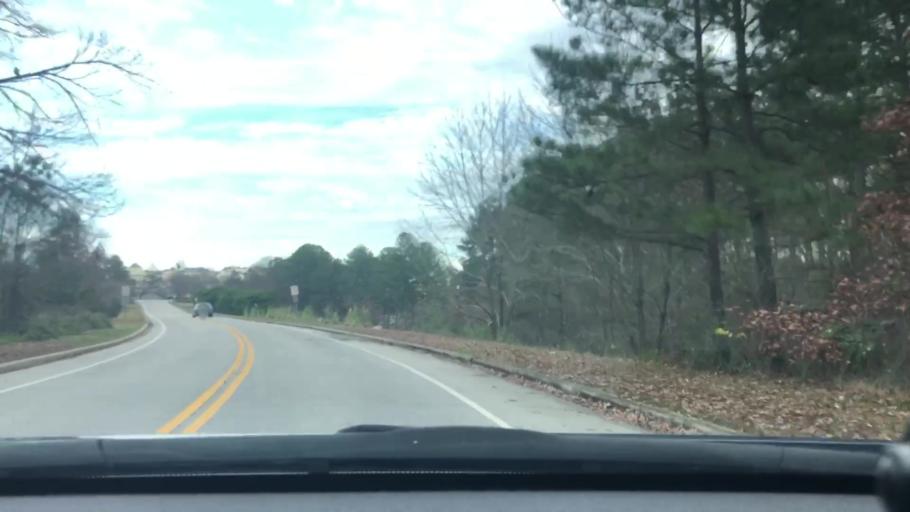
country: US
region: South Carolina
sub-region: Lexington County
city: Irmo
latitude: 34.0766
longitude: -81.1636
